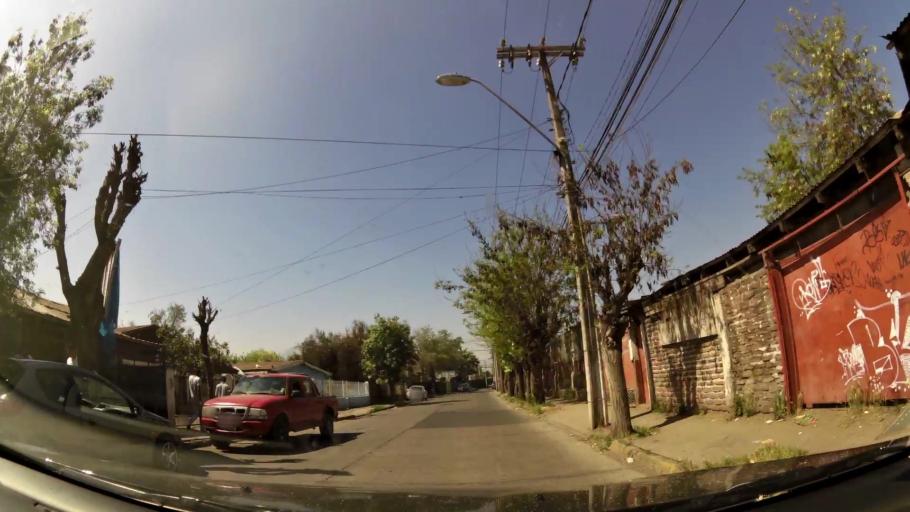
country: CL
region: Santiago Metropolitan
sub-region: Provincia de Santiago
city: Lo Prado
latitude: -33.3690
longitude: -70.7151
